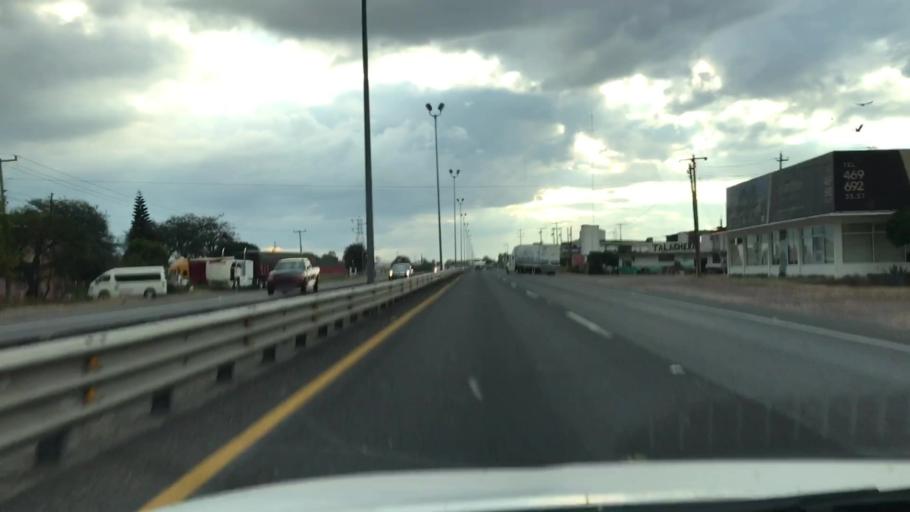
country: MX
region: Guanajuato
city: Penjamo
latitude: 20.4299
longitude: -101.7052
